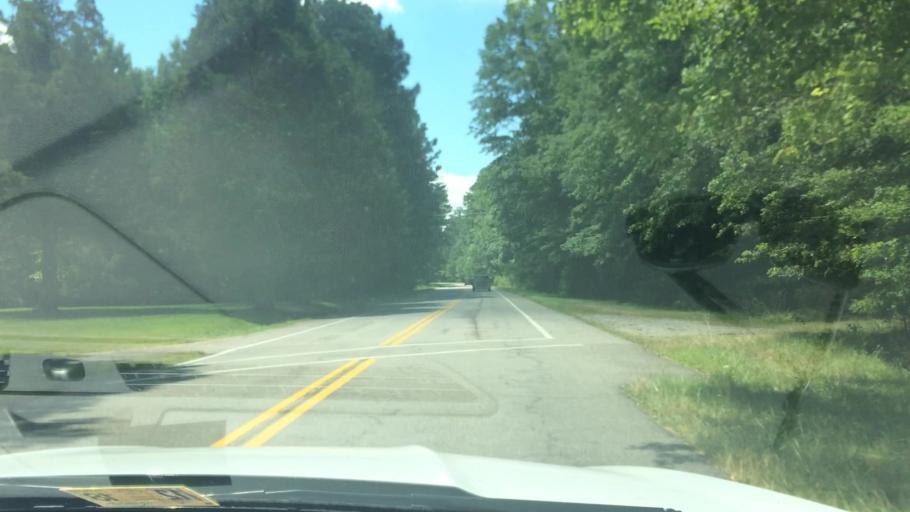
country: US
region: Virginia
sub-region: King William County
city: West Point
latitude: 37.5521
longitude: -76.7935
